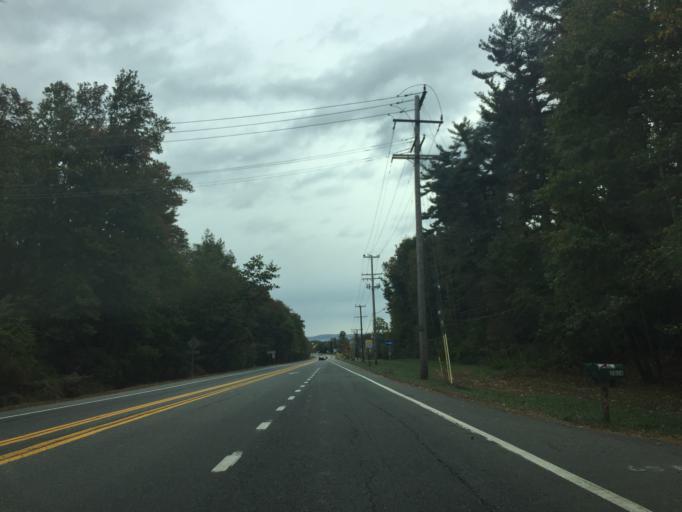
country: US
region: Maryland
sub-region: Harford County
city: Havre de Grace
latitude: 39.5666
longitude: -76.1284
